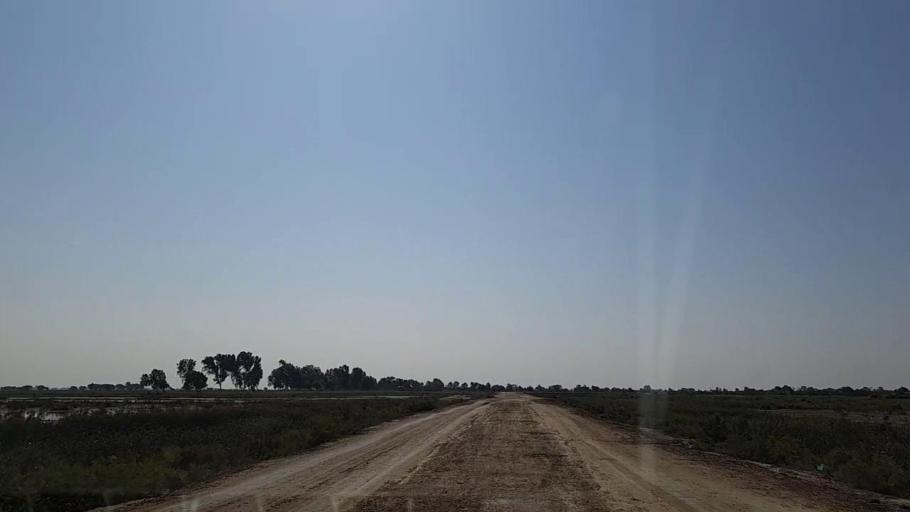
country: PK
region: Sindh
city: Chuhar Jamali
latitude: 24.5015
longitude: 68.0985
